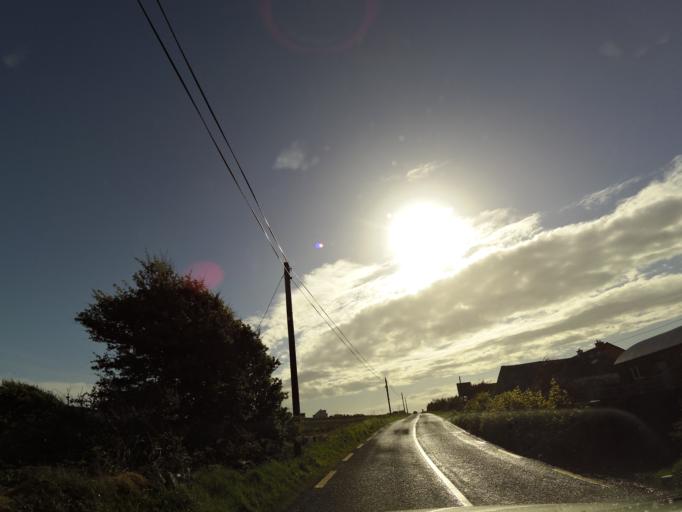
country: IE
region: Connaught
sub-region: County Galway
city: Bearna
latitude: 53.0048
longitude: -9.3664
